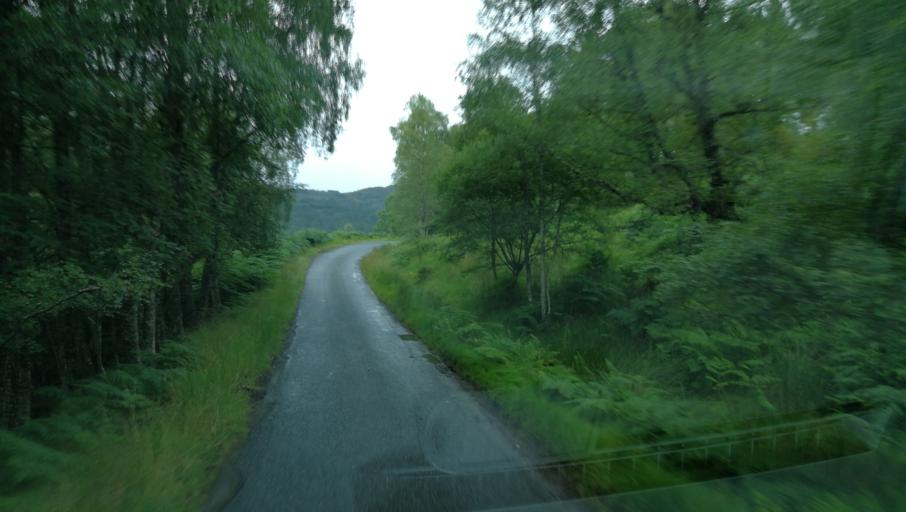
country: GB
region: Scotland
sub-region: Highland
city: Spean Bridge
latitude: 57.2864
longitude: -4.9213
